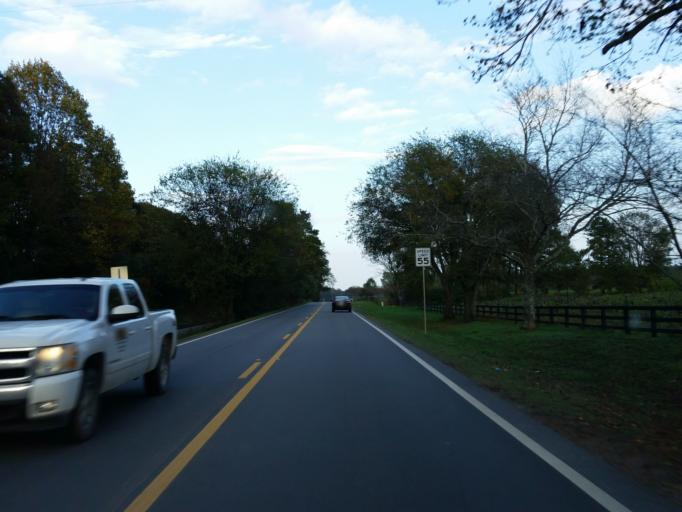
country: US
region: Georgia
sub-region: Monroe County
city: Forsyth
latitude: 32.9505
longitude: -83.8240
